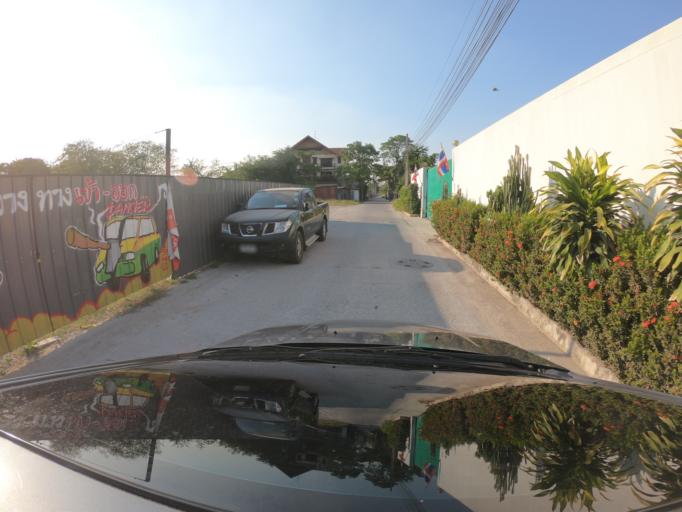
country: TH
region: Bangkok
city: Bang Na
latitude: 13.6447
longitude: 100.6351
